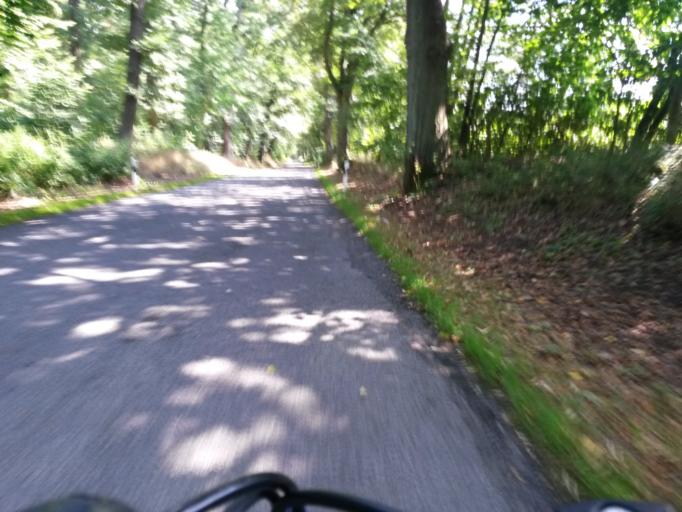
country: DE
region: Brandenburg
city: Angermunde
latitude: 53.0084
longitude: 13.9238
